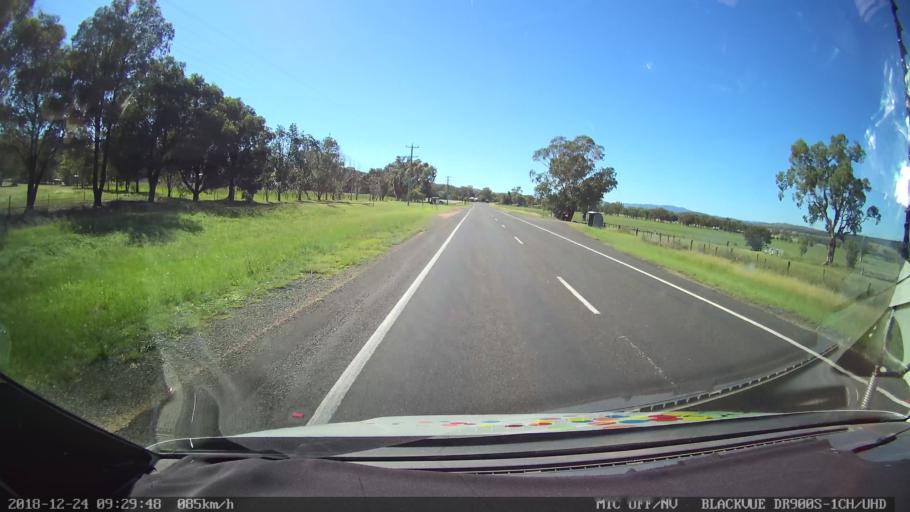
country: AU
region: New South Wales
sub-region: Liverpool Plains
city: Quirindi
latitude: -31.5554
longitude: 150.6934
